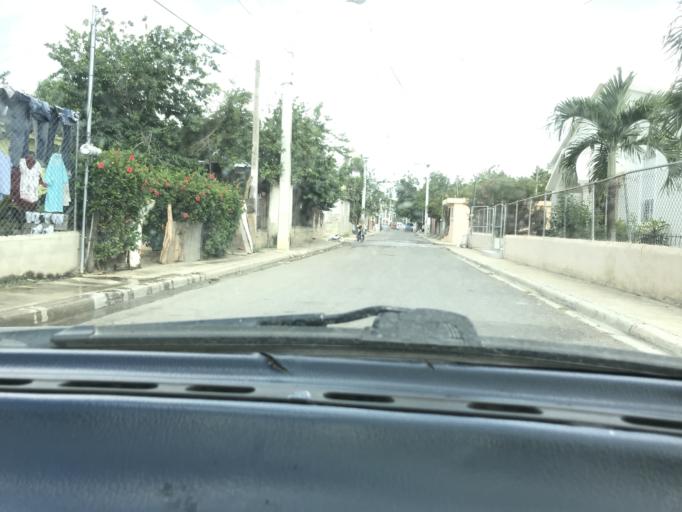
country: DO
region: Santiago
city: Santiago de los Caballeros
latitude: 19.4508
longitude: -70.7301
